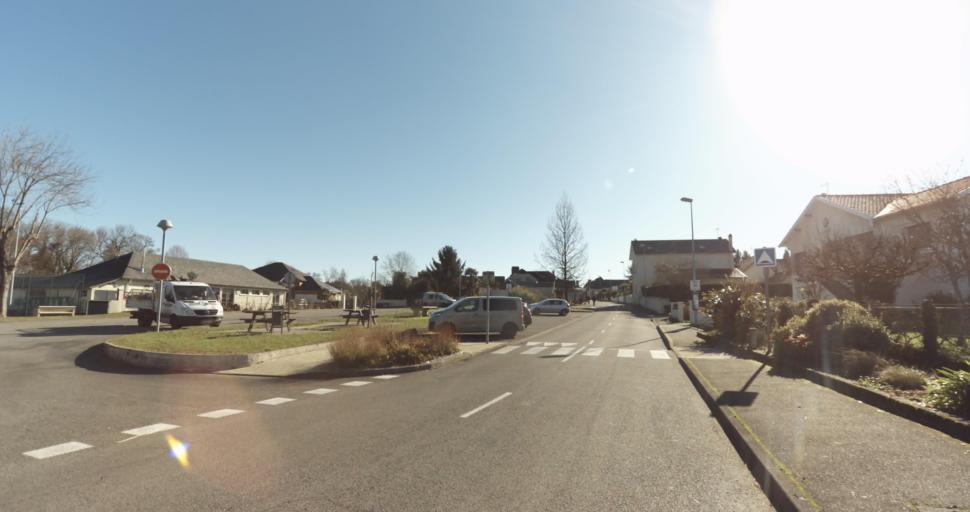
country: FR
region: Aquitaine
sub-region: Departement des Pyrenees-Atlantiques
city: Morlaas
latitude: 43.3494
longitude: -0.2628
